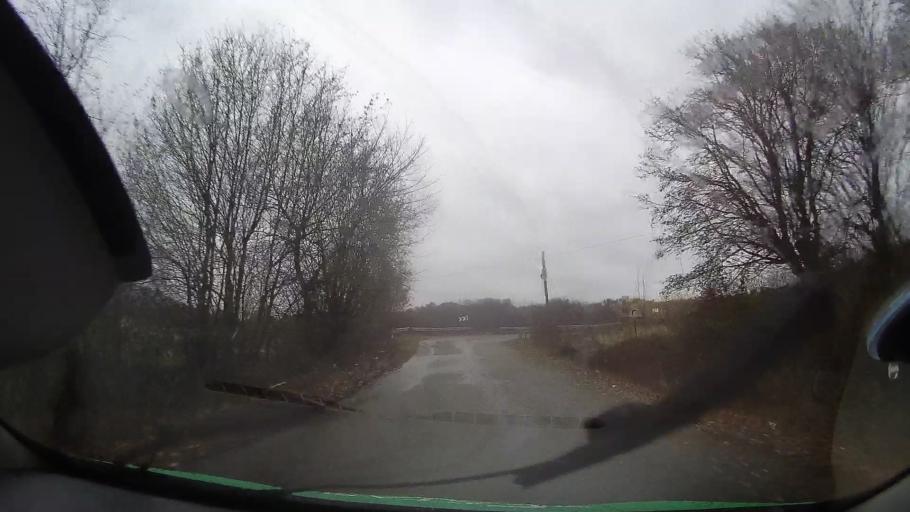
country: RO
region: Bihor
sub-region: Comuna Rabagani
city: Rabagani
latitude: 46.7267
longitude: 22.2399
